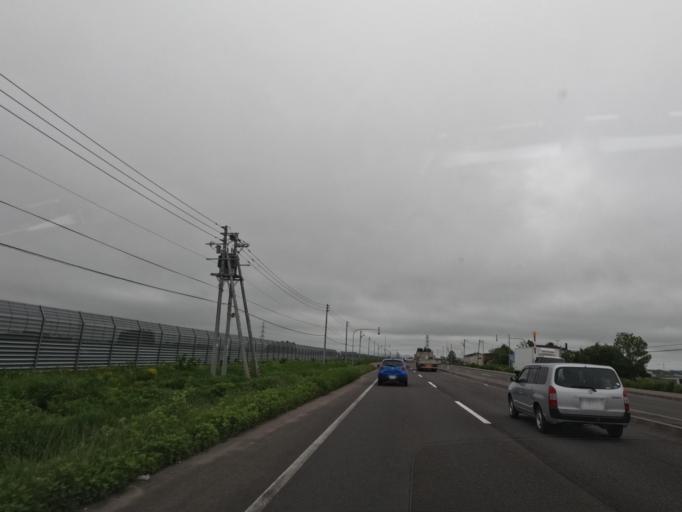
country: JP
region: Hokkaido
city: Ebetsu
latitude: 43.1533
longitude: 141.5182
